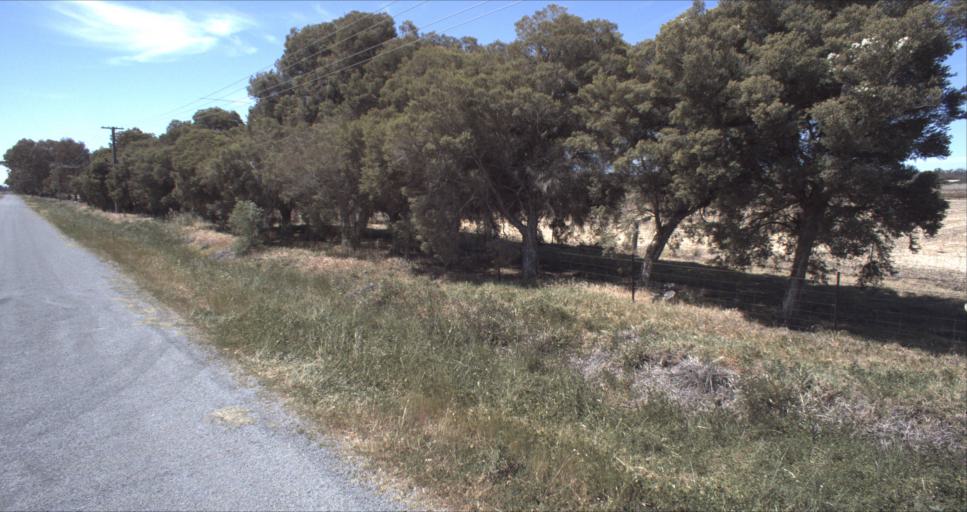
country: AU
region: New South Wales
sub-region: Leeton
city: Leeton
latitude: -34.5831
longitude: 146.4201
